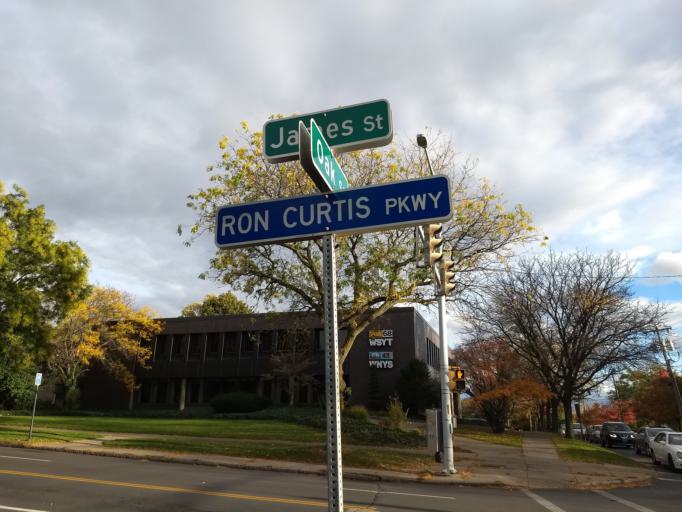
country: US
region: New York
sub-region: Onondaga County
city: Syracuse
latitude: 43.0593
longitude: -76.1345
